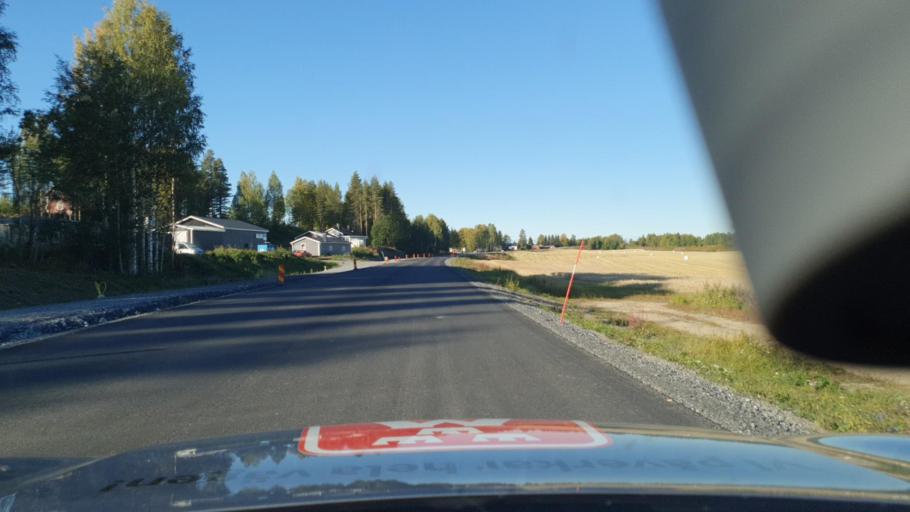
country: SE
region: Norrbotten
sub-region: Alvsbyns Kommun
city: AElvsbyn
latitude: 65.6685
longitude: 20.9027
